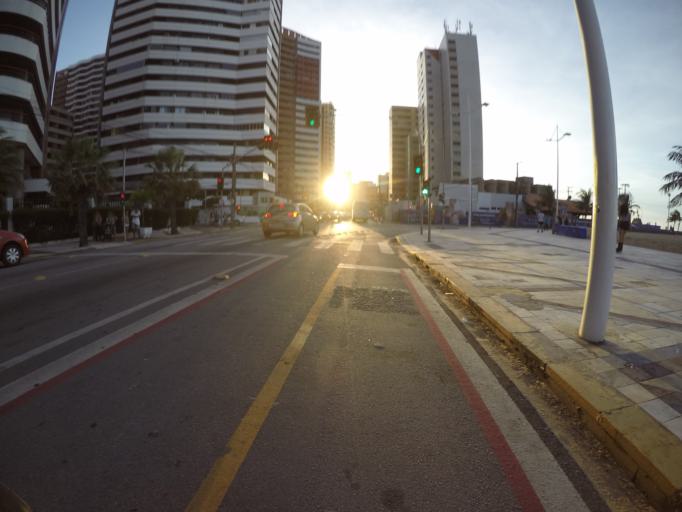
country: BR
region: Ceara
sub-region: Fortaleza
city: Fortaleza
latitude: -3.7217
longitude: -38.5092
